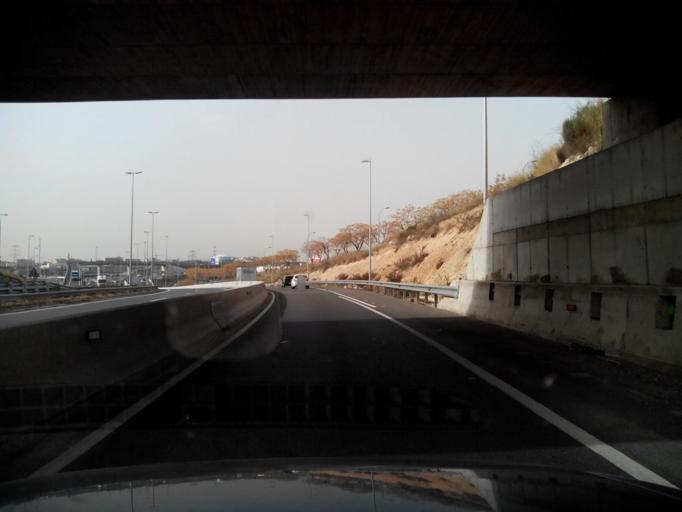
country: ES
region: Catalonia
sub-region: Provincia de Tarragona
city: Constanti
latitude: 41.1317
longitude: 1.2064
